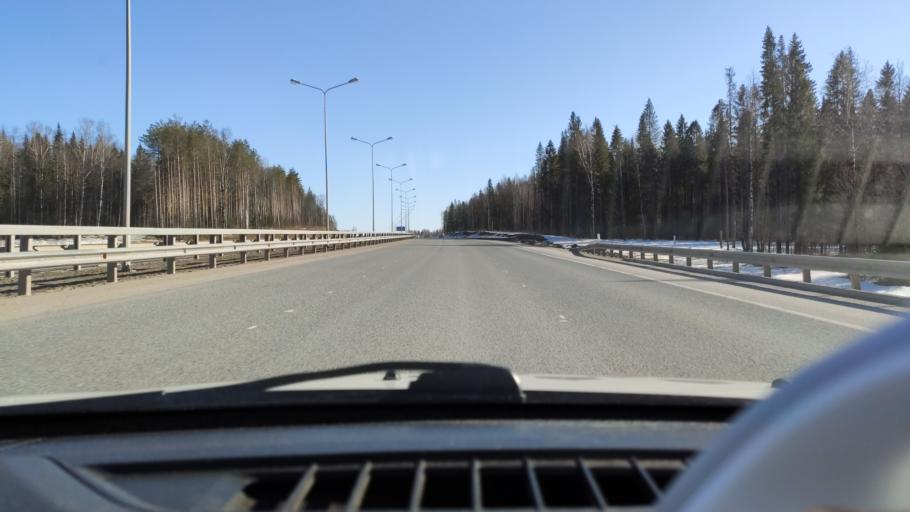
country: RU
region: Perm
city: Zvezdnyy
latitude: 57.7460
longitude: 56.3349
